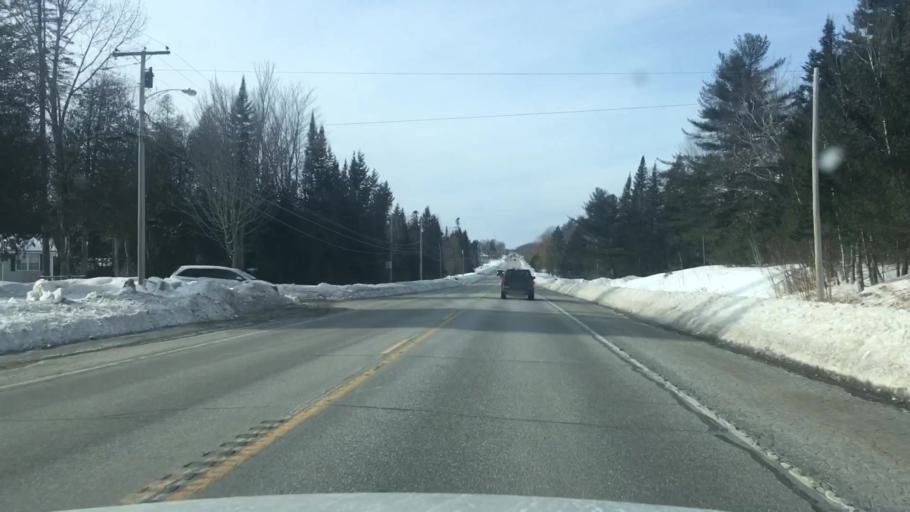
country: US
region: Maine
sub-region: Penobscot County
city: Kenduskeag
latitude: 44.9768
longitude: -68.9888
